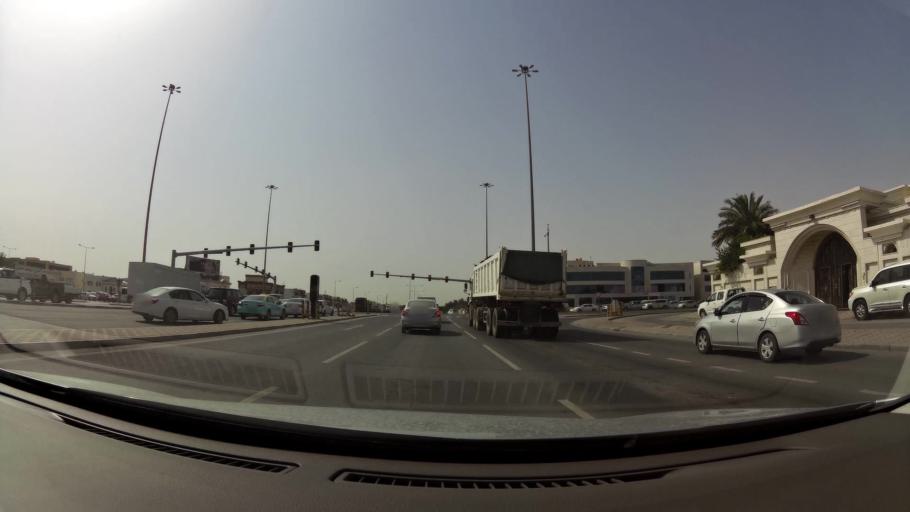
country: QA
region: Baladiyat ad Dawhah
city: Doha
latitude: 25.2550
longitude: 51.5241
